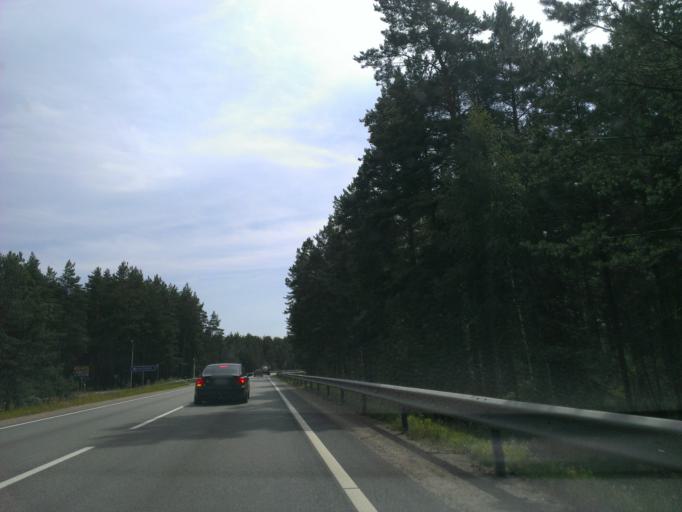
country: LV
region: Riga
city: Bergi
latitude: 56.9604
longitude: 24.3746
